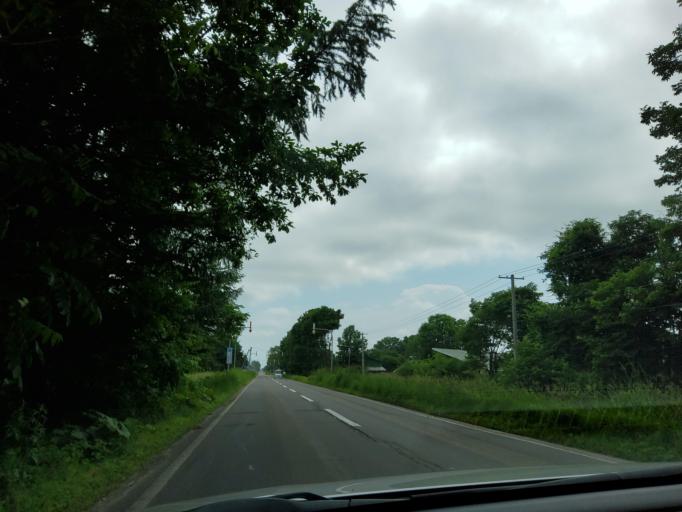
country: JP
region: Hokkaido
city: Obihiro
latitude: 42.9035
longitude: 143.1247
